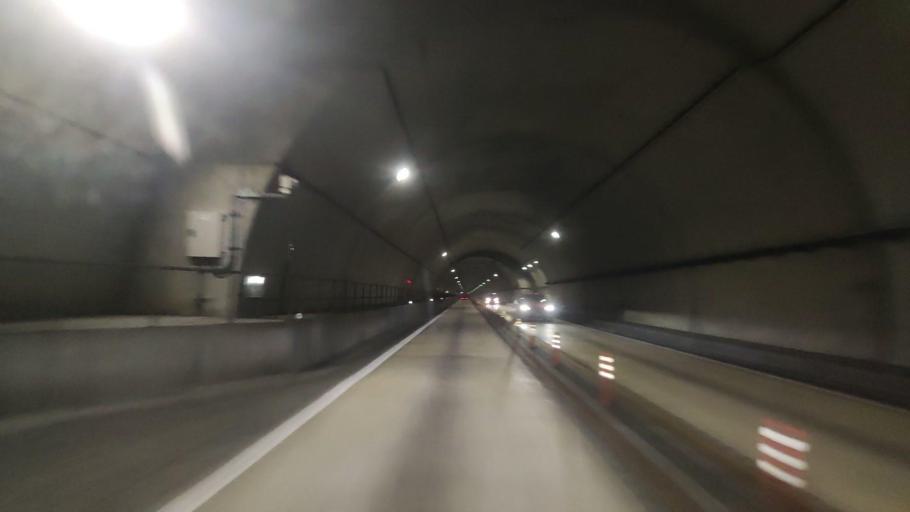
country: JP
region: Wakayama
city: Tanabe
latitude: 33.5694
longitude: 135.4861
